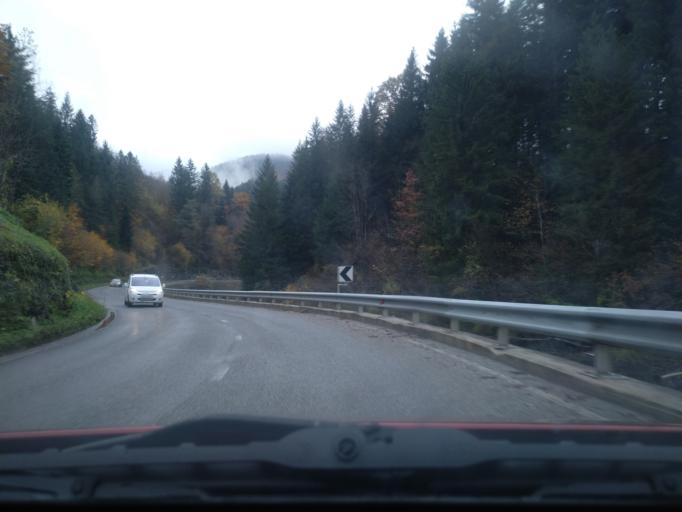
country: SI
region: Luce
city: Luce
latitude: 46.3593
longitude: 14.7603
